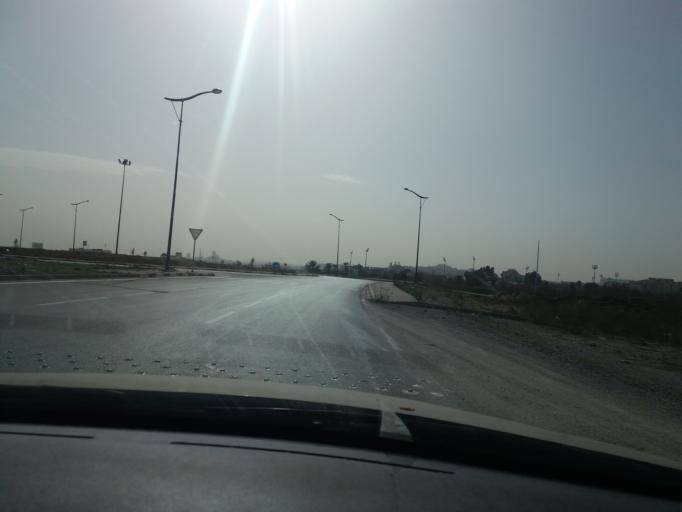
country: TN
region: Tunis
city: Tunis
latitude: 36.8078
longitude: 10.1933
